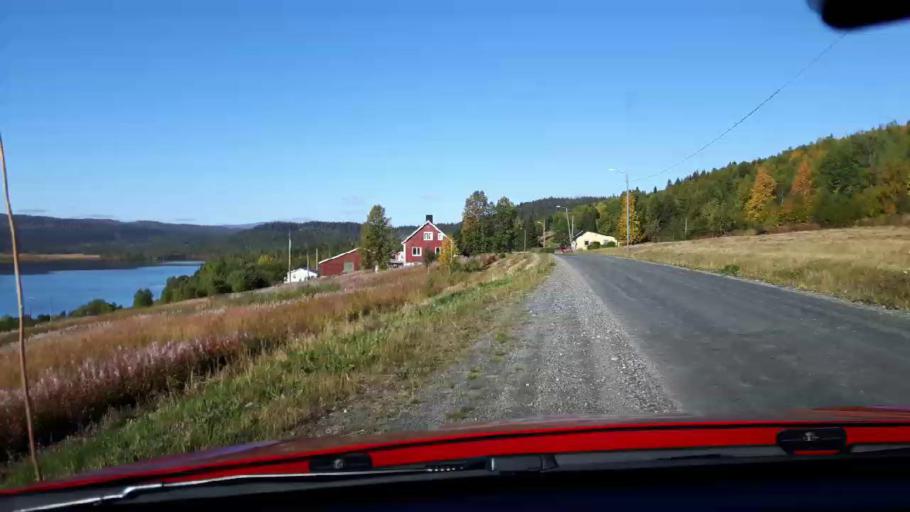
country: NO
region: Nord-Trondelag
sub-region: Lierne
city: Sandvika
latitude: 64.6072
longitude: 13.7760
